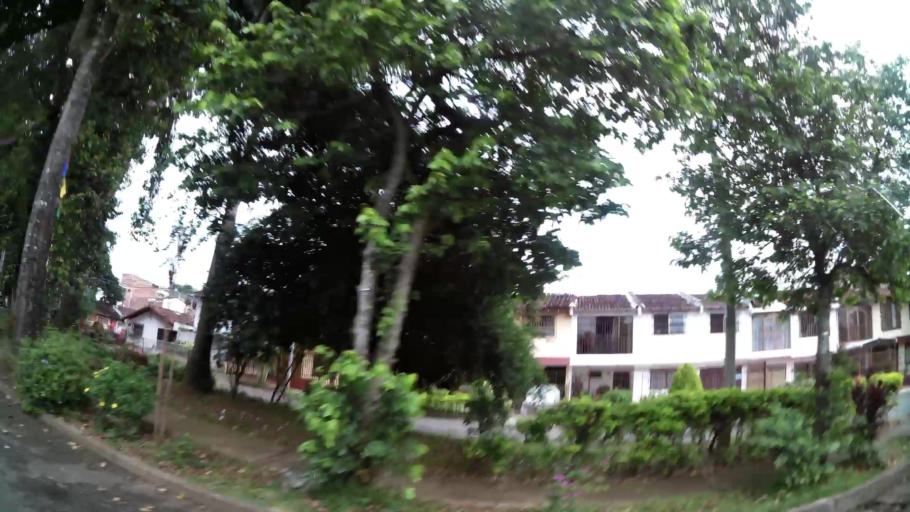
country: CO
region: Valle del Cauca
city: Cali
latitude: 3.3885
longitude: -76.5398
